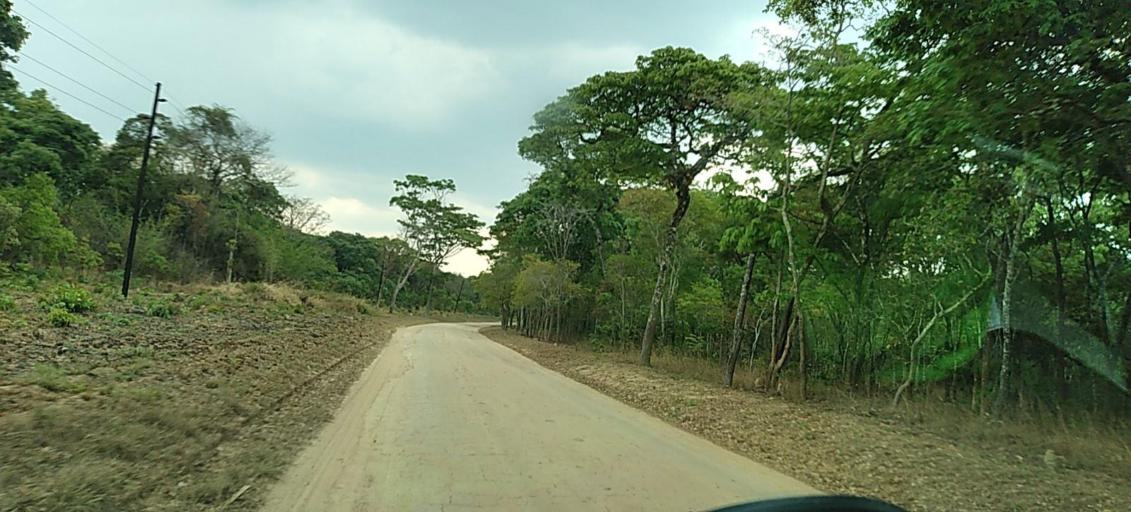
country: ZM
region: North-Western
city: Solwezi
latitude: -12.7744
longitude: 26.4705
